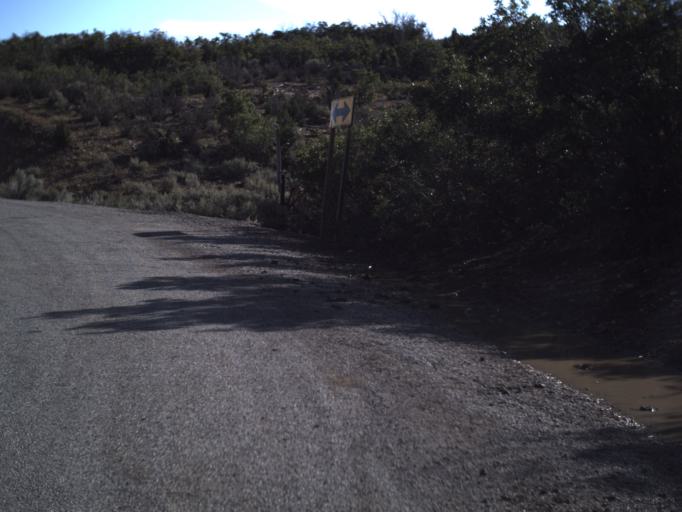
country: US
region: Utah
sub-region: Millard County
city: Fillmore
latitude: 39.2014
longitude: -112.1729
